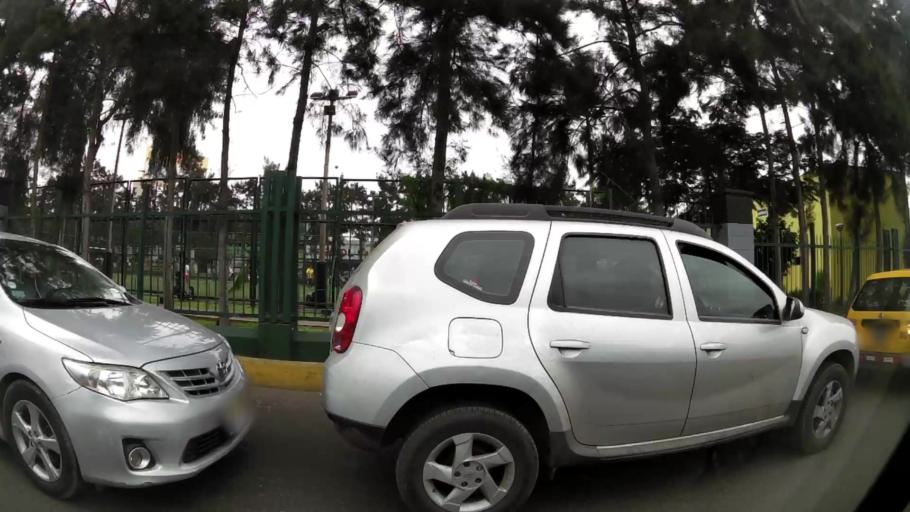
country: PE
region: Lima
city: Lima
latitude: -12.0438
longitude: -77.0493
